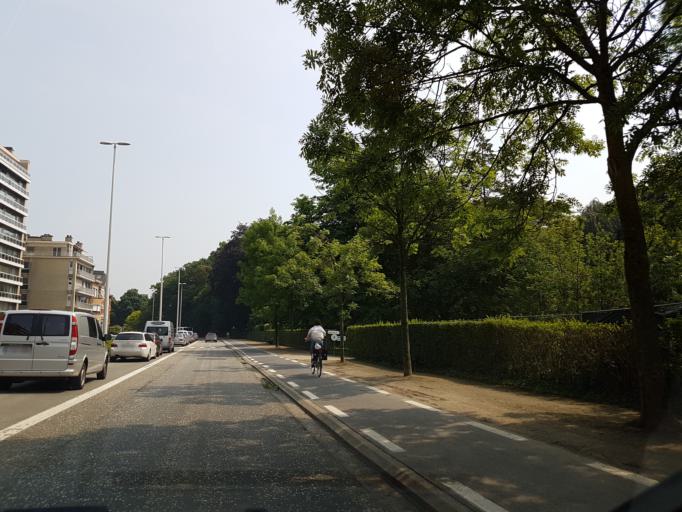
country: BE
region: Flanders
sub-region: Provincie Oost-Vlaanderen
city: Aalst
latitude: 50.9313
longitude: 4.0439
